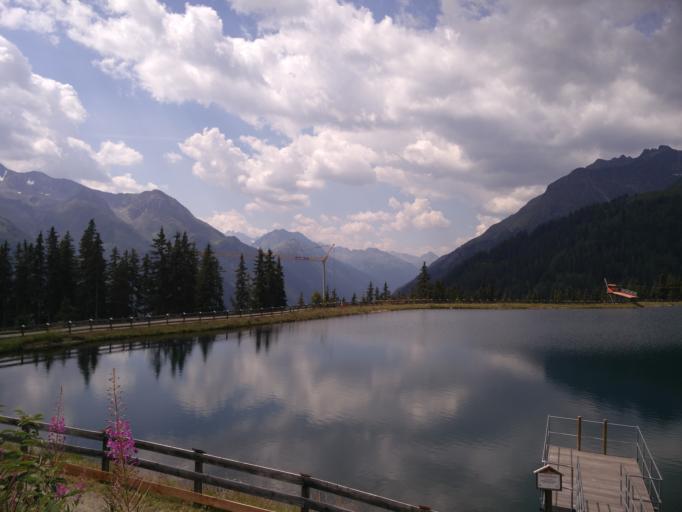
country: AT
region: Tyrol
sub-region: Politischer Bezirk Landeck
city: Kappl
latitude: 47.0661
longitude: 10.3568
